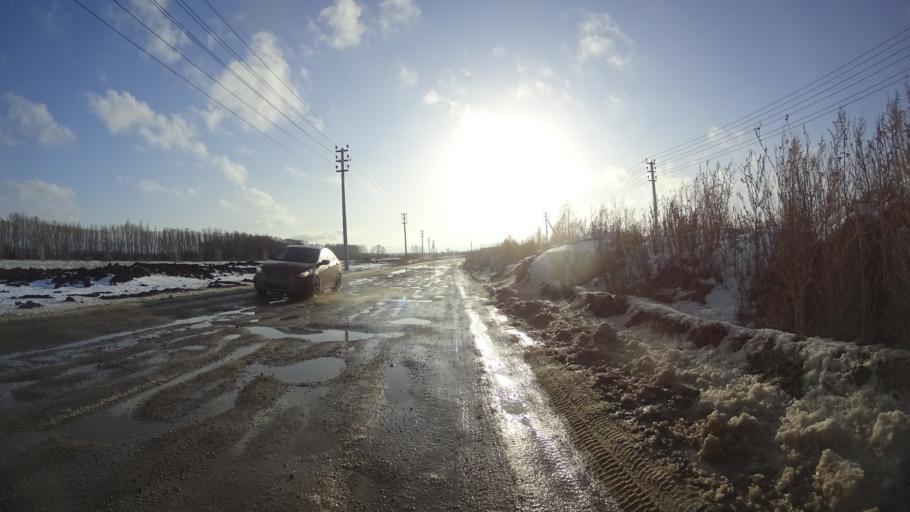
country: RU
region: Chelyabinsk
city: Sargazy
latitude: 55.1067
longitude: 61.2686
